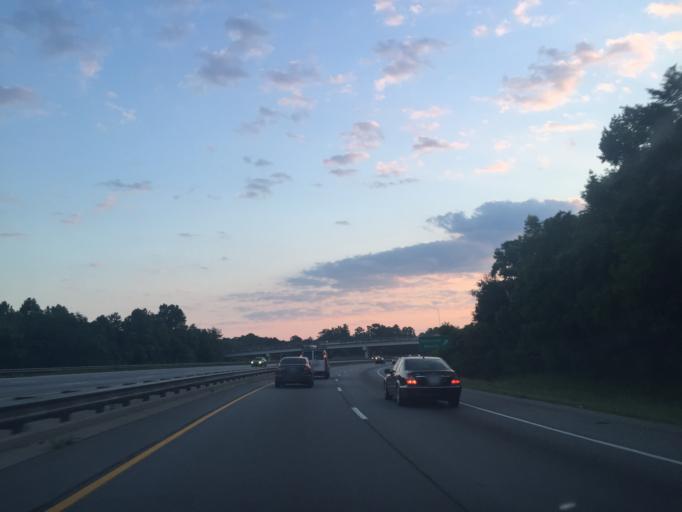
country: US
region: Georgia
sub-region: Chatham County
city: Thunderbolt
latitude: 32.0324
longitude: -81.0845
